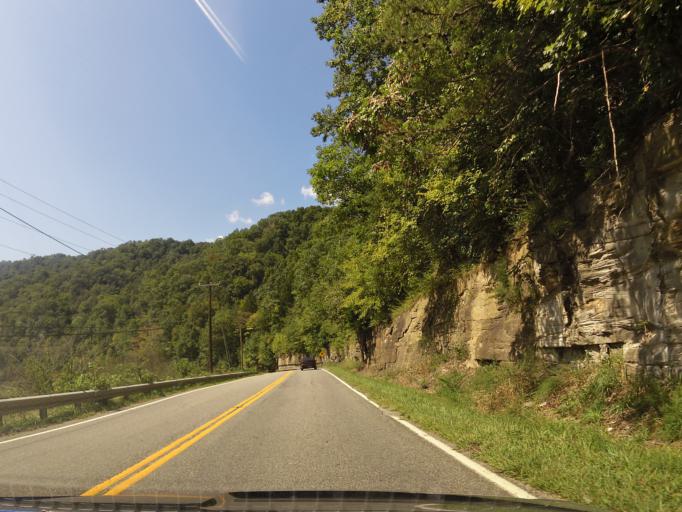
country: US
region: Kentucky
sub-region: Leslie County
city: Hyden
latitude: 37.1487
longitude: -83.3779
